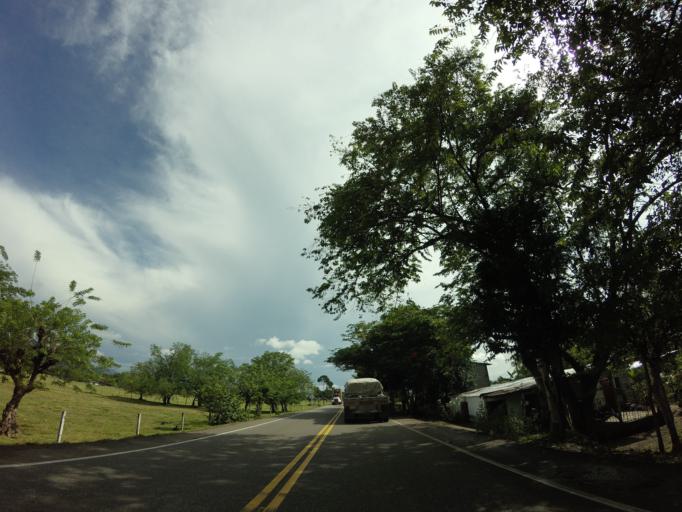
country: CO
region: Tolima
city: Honda
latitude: 5.3234
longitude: -74.7395
